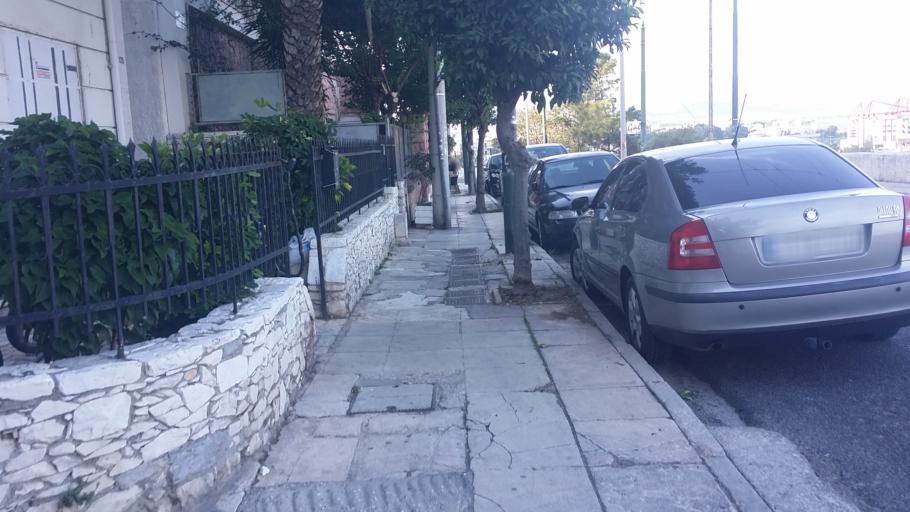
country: GR
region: Attica
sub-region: Nomarchia Athinas
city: Moskhaton
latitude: 37.9407
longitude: 23.6614
